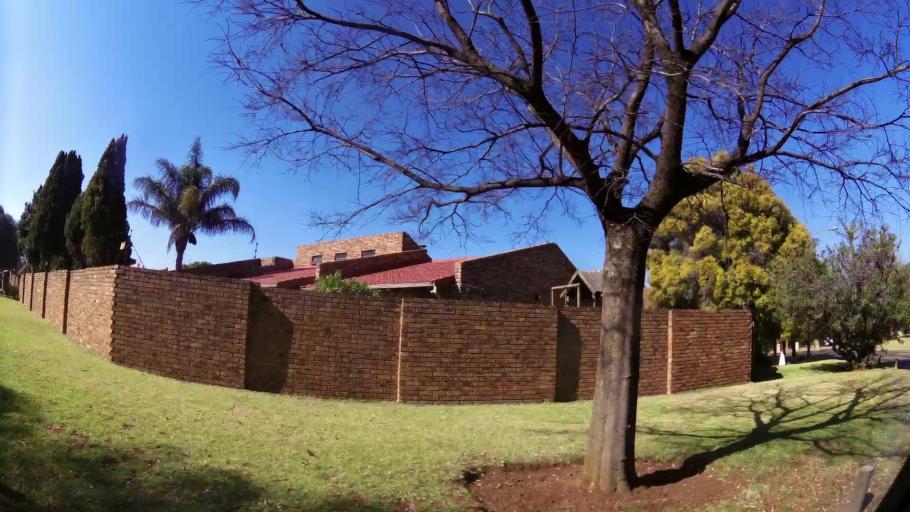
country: ZA
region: Gauteng
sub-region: Ekurhuleni Metropolitan Municipality
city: Germiston
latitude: -26.3004
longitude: 28.0999
